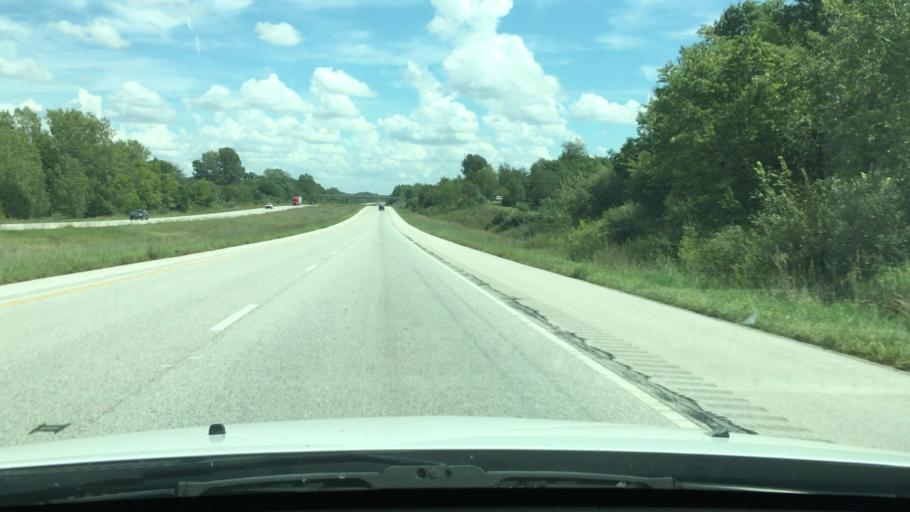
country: US
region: Illinois
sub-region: Scott County
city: Winchester
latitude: 39.6812
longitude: -90.4230
